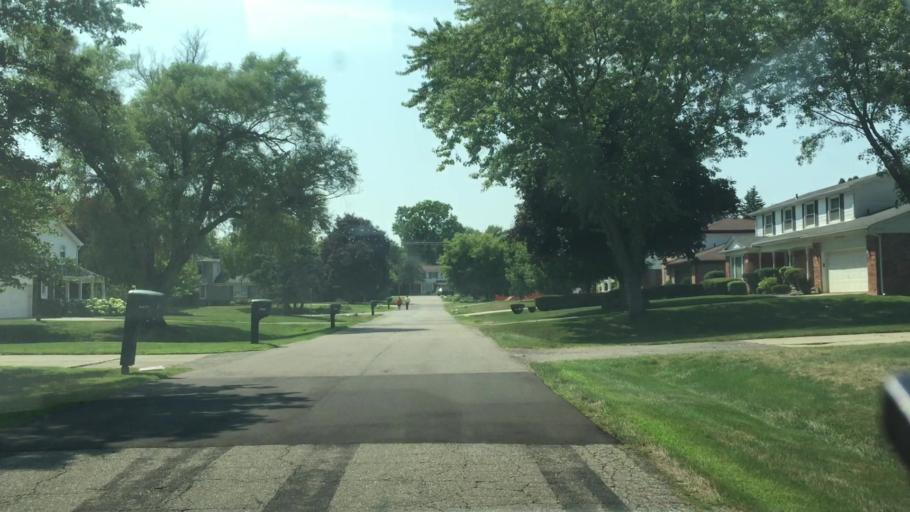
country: US
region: Michigan
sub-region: Oakland County
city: Orchard Lake
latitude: 42.5407
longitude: -83.3491
